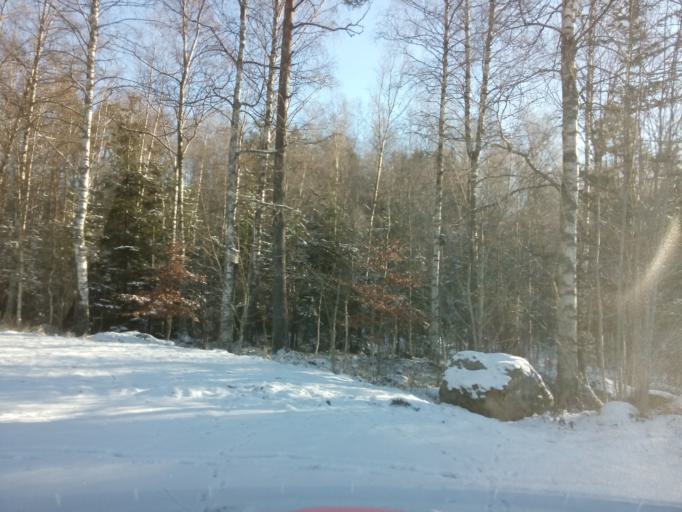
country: SE
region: Vaestra Goetaland
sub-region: Boras Kommun
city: Ganghester
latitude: 57.8326
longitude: 13.0132
